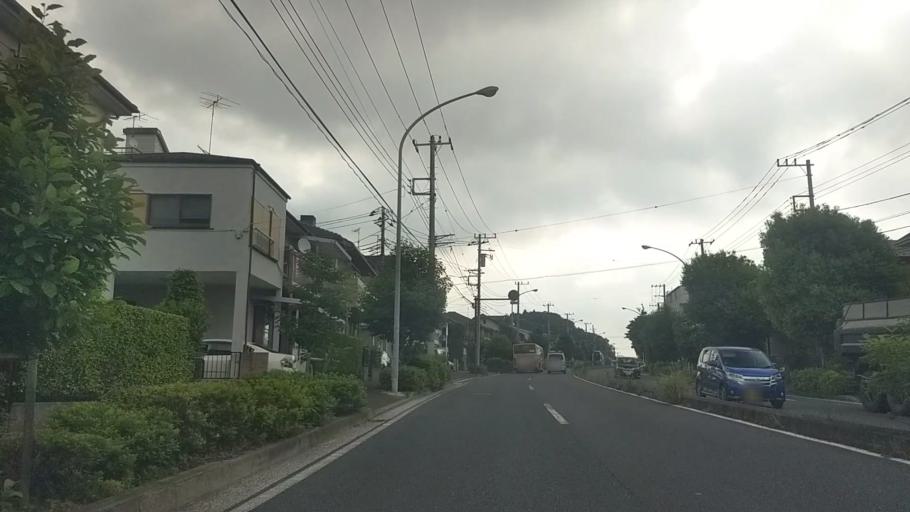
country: JP
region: Kanagawa
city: Kamakura
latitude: 35.3799
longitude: 139.5411
